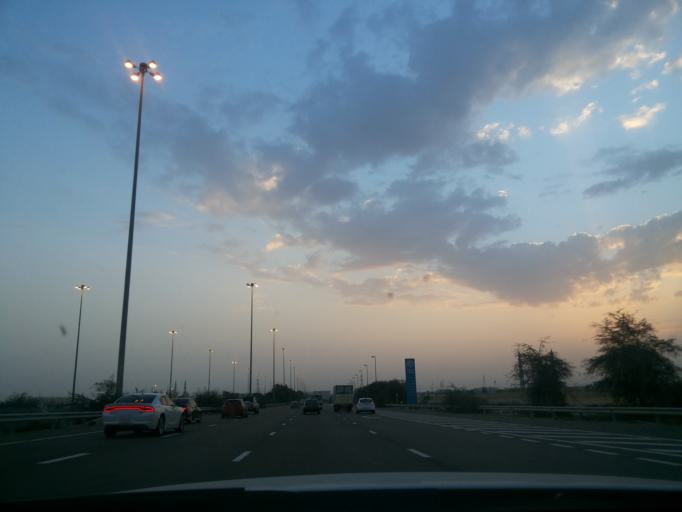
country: AE
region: Abu Dhabi
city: Abu Dhabi
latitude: 24.6761
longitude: 54.7650
